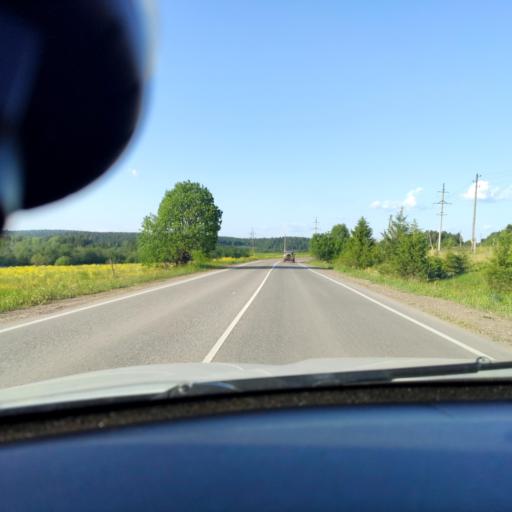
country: RU
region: Perm
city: Bershet'
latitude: 57.8141
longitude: 56.4738
